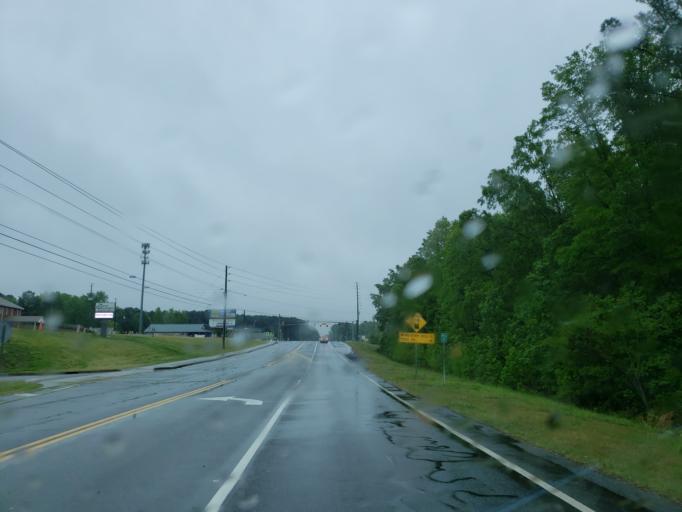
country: US
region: Georgia
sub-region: Carroll County
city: Villa Rica
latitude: 33.8072
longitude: -84.8910
